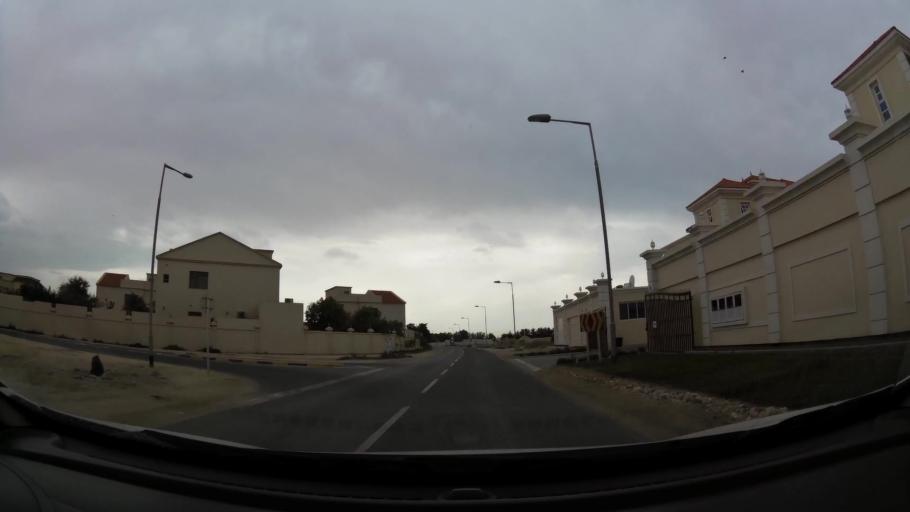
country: BH
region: Central Governorate
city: Madinat Hamad
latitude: 26.1468
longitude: 50.4728
